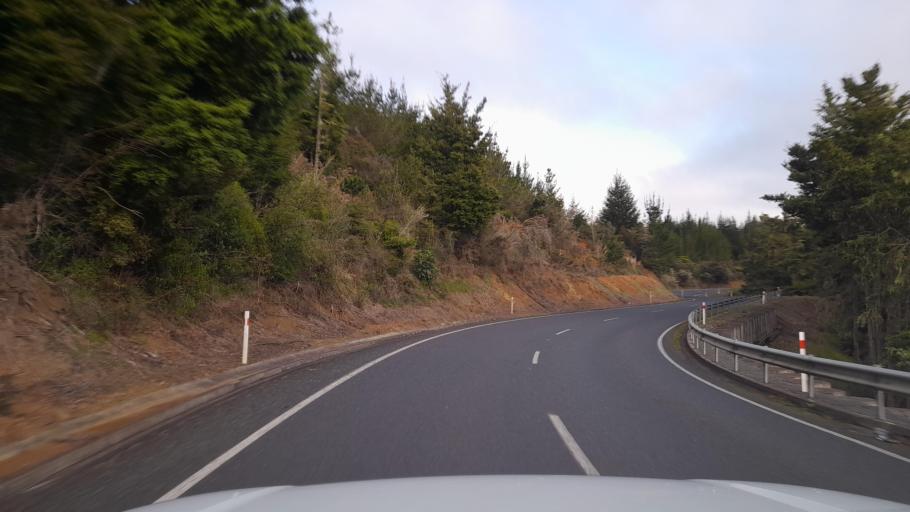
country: NZ
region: Northland
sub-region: Far North District
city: Waimate North
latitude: -35.5102
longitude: 173.8379
